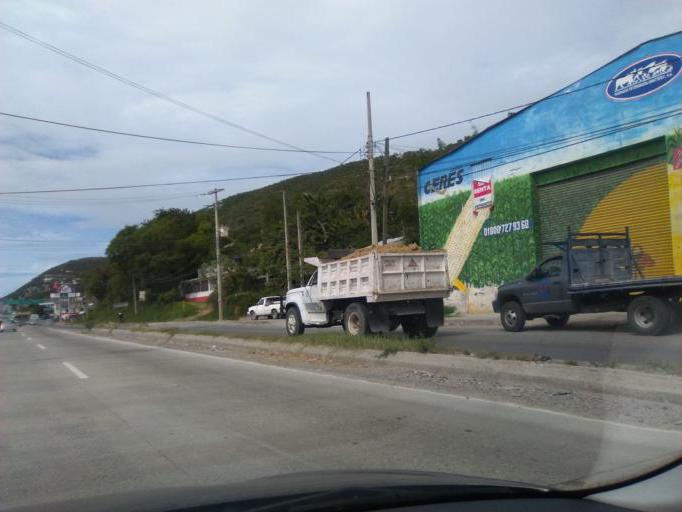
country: MX
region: Guerrero
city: Chilpancingo de los Bravos
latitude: 17.5728
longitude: -99.5128
